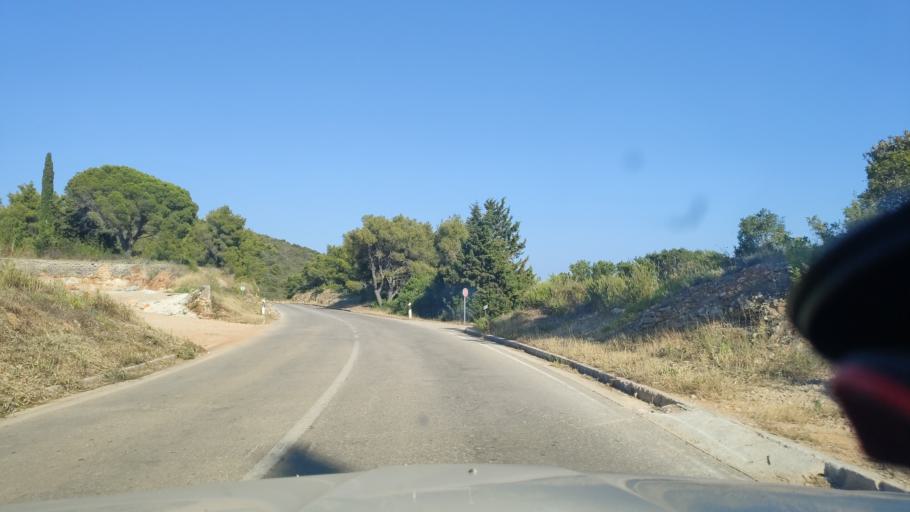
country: HR
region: Splitsko-Dalmatinska
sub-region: Grad Vis
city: Vis
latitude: 43.0320
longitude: 16.2028
